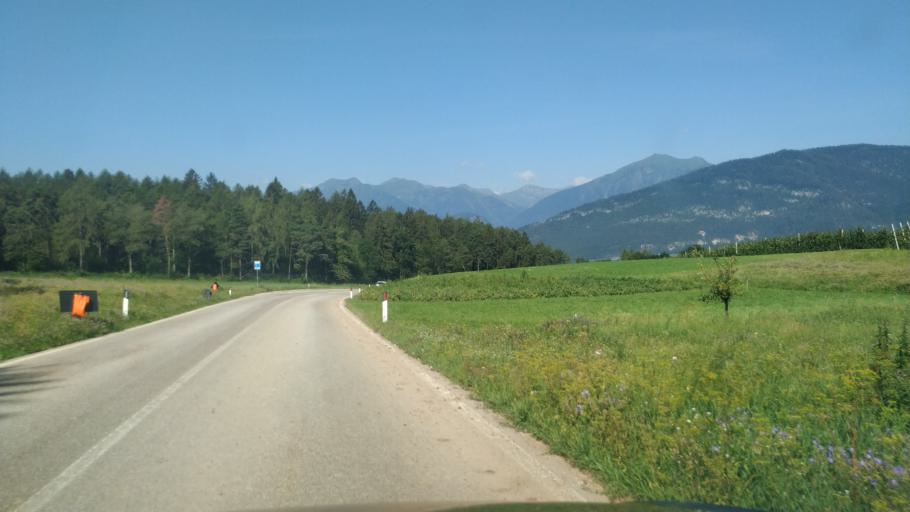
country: IT
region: Trentino-Alto Adige
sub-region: Provincia di Trento
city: Romeno
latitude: 46.3893
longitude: 11.1096
